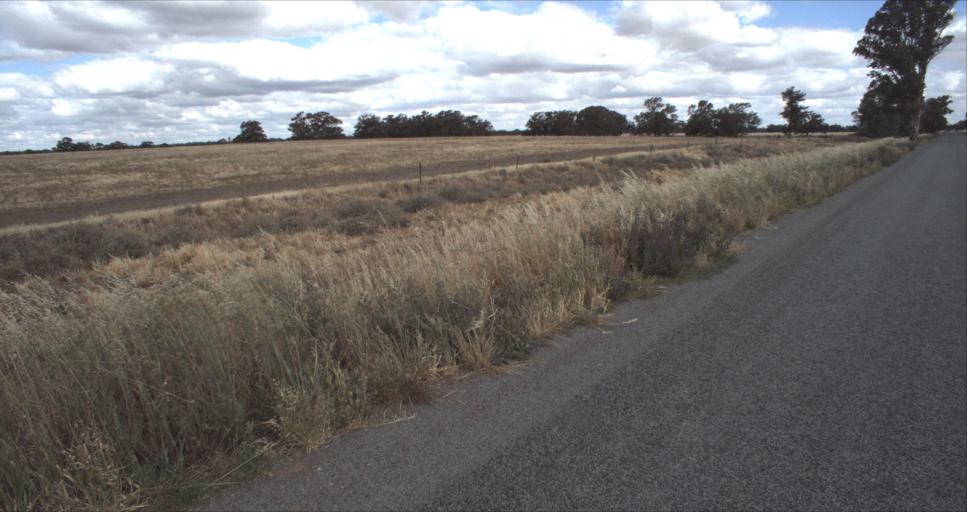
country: AU
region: New South Wales
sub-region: Leeton
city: Leeton
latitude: -34.6888
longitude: 146.3441
